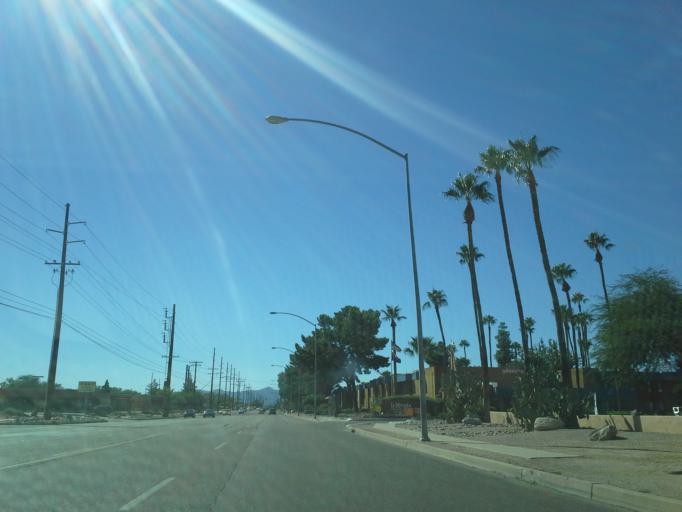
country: US
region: Arizona
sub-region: Pima County
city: Tucson
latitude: 32.2507
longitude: -110.8964
